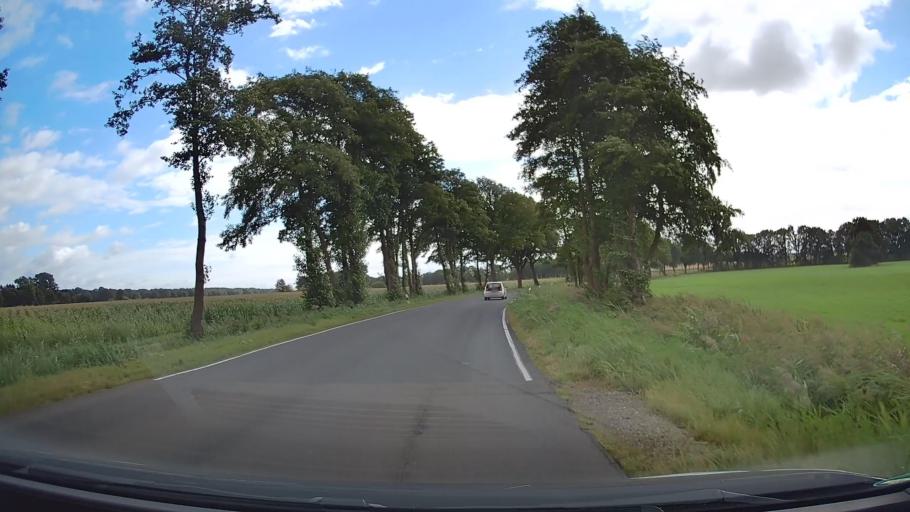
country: DE
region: Lower Saxony
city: Rhade
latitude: 53.3245
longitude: 9.1234
